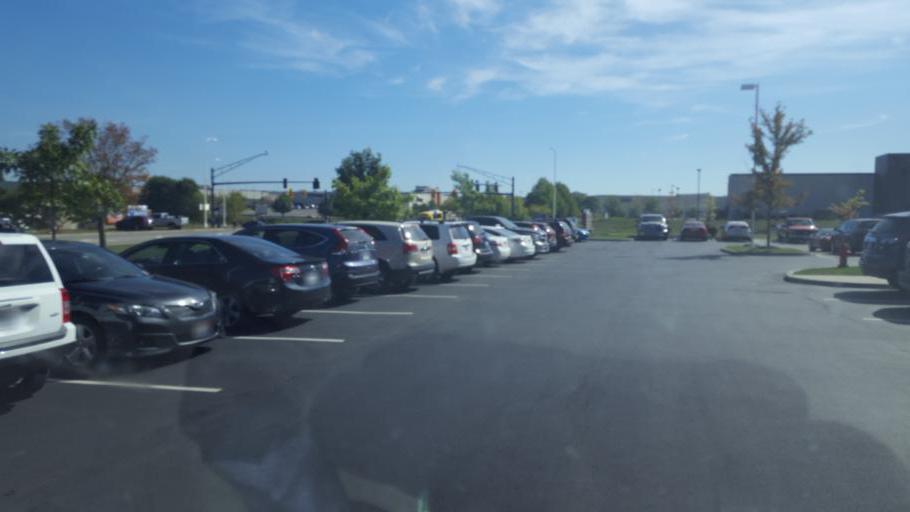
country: US
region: Ohio
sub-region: Delaware County
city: Lewis Center
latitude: 40.1492
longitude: -82.9849
